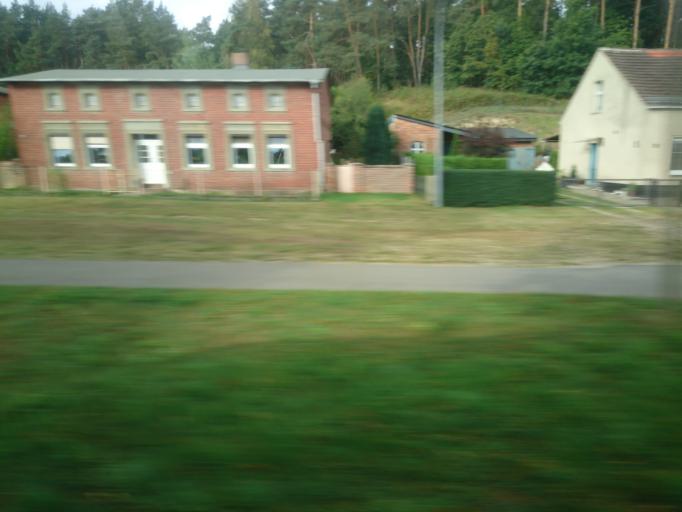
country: DE
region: Mecklenburg-Vorpommern
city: Jatznick
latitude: 53.5524
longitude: 13.9684
